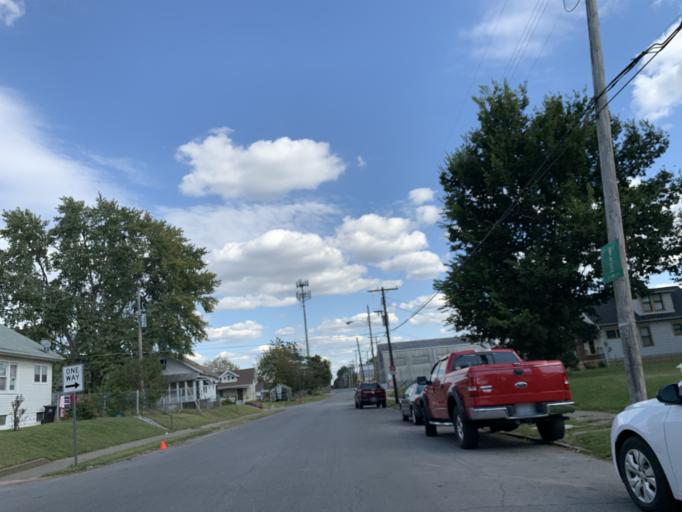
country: US
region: Indiana
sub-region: Floyd County
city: New Albany
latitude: 38.2455
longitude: -85.8048
